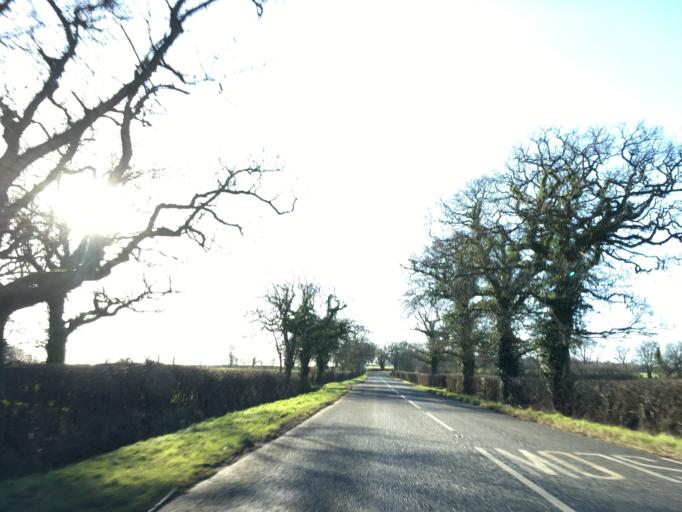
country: GB
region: England
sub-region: Wiltshire
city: Minety
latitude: 51.6100
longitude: -1.9685
